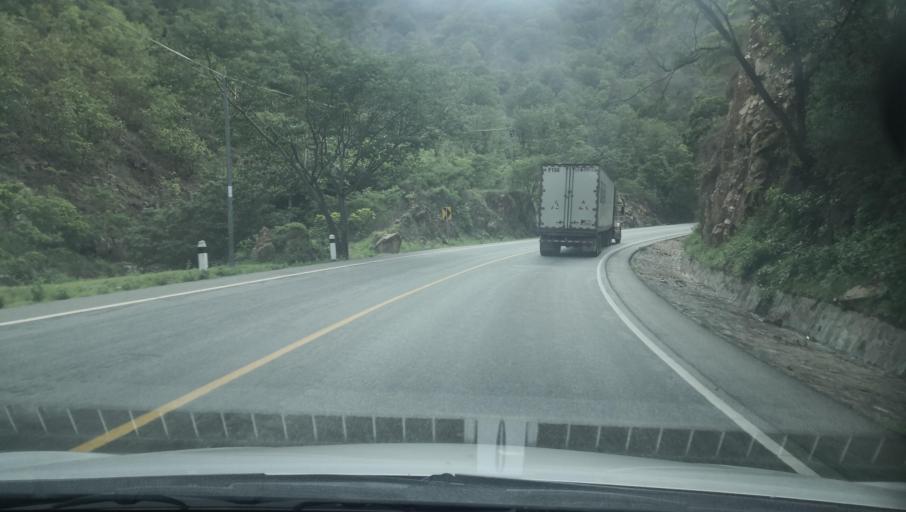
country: NI
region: Nueva Segovia
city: Mozonte
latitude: 13.7114
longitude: -86.5037
